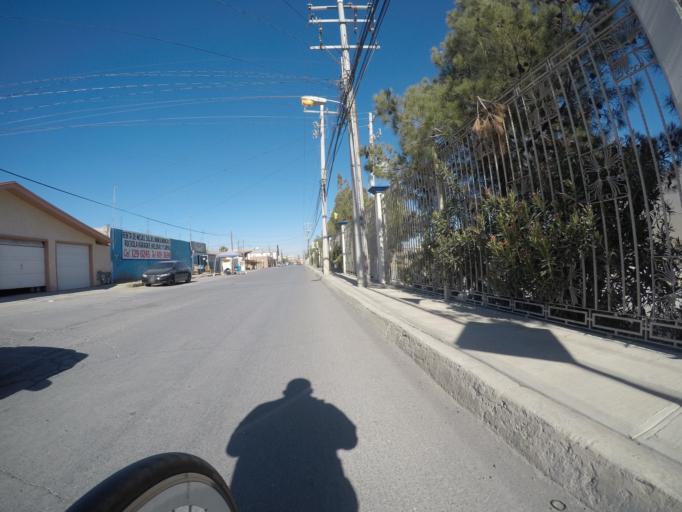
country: MX
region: Chihuahua
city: Ciudad Juarez
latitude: 31.7077
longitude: -106.4135
